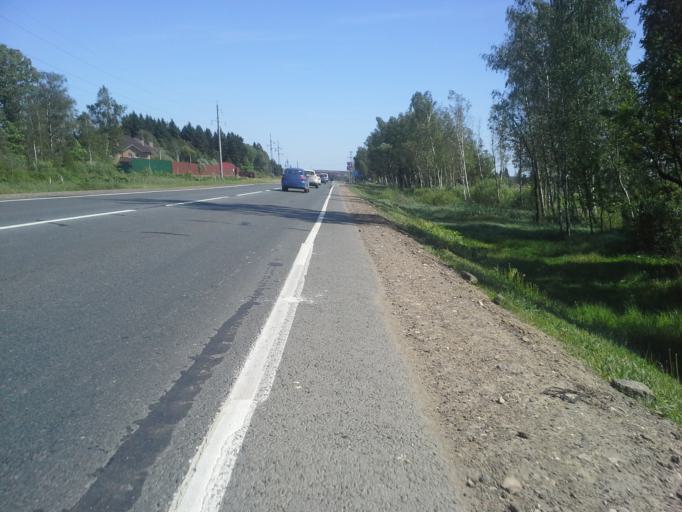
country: RU
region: Moskovskaya
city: Troitsk
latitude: 55.4256
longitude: 37.1753
